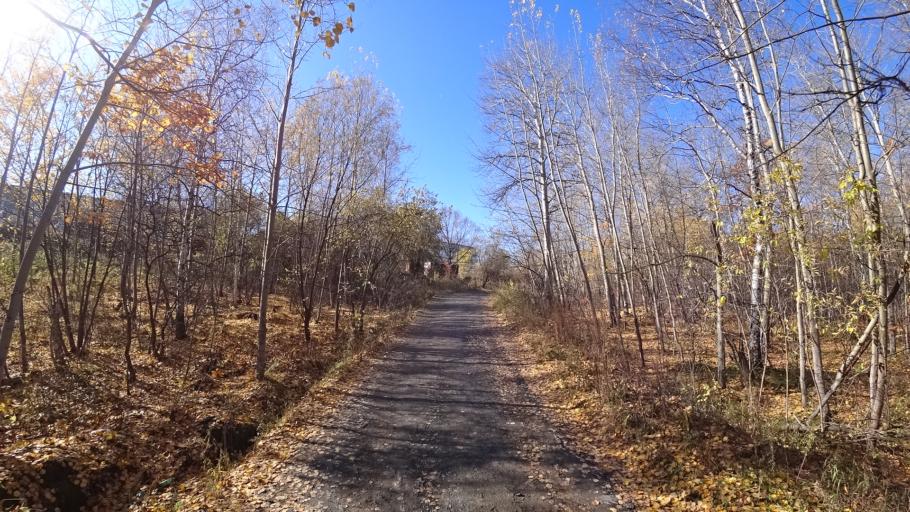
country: RU
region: Khabarovsk Krai
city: Amursk
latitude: 50.2224
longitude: 136.9107
